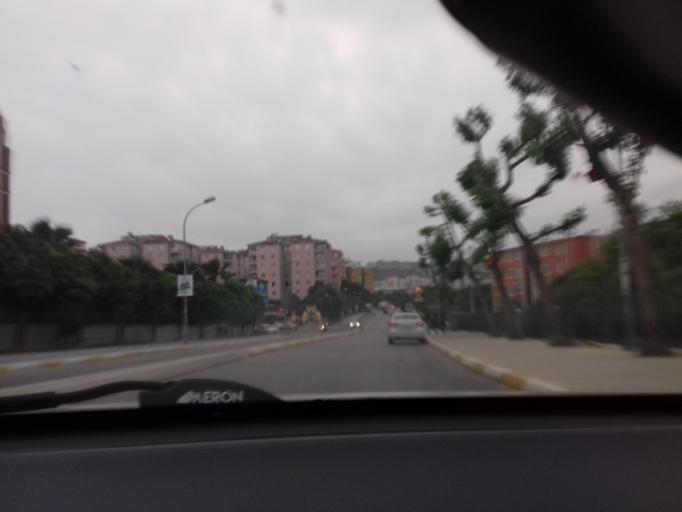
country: TR
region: Istanbul
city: Sultanbeyli
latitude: 40.9278
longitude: 29.2964
